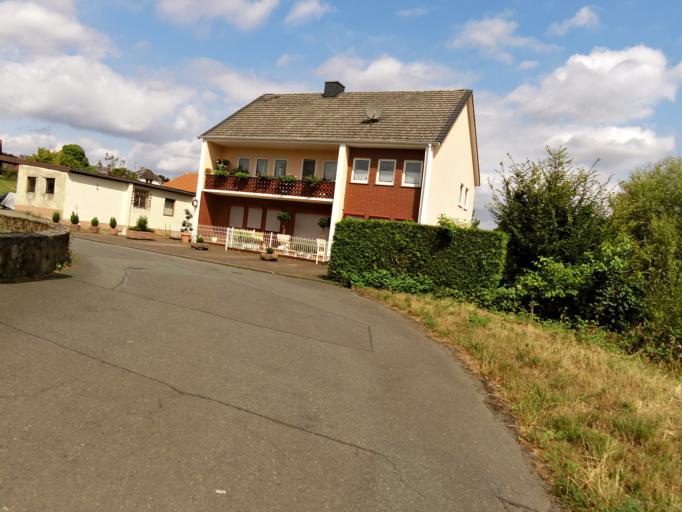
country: DE
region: Hesse
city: Reichelsheim
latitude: 49.7193
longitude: 8.8657
